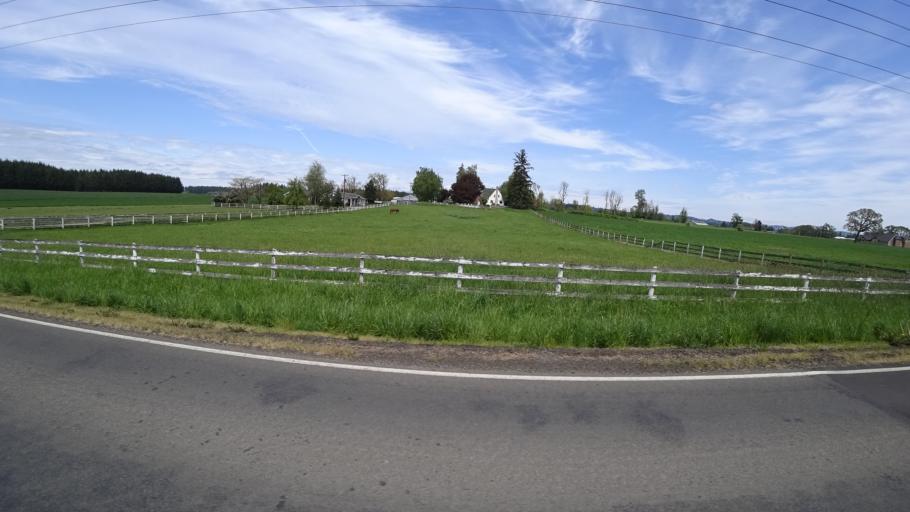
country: US
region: Oregon
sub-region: Washington County
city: Rockcreek
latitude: 45.5783
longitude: -122.9273
